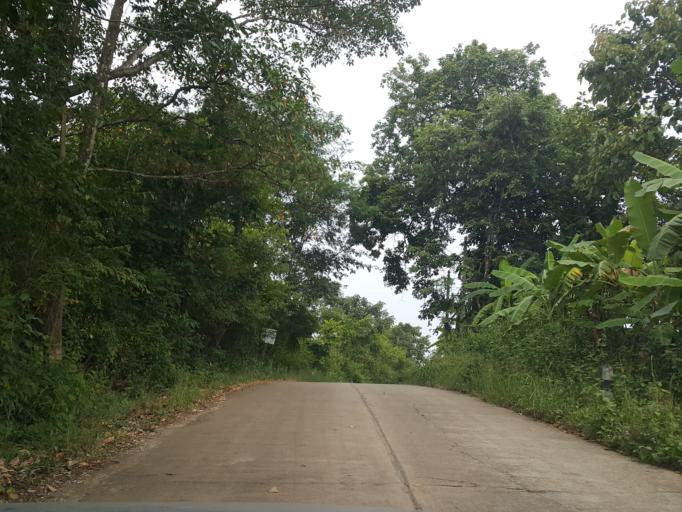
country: TH
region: Mae Hong Son
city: Wiang Nuea
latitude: 19.3686
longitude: 98.4496
